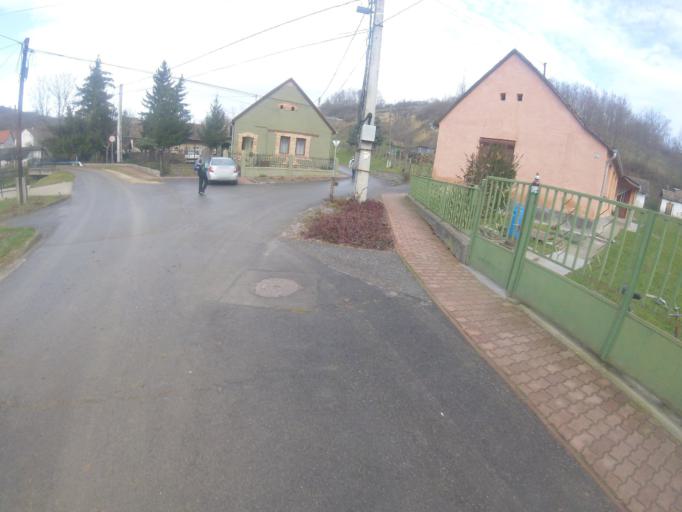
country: HU
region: Tolna
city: Bonyhad
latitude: 46.2227
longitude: 18.5974
